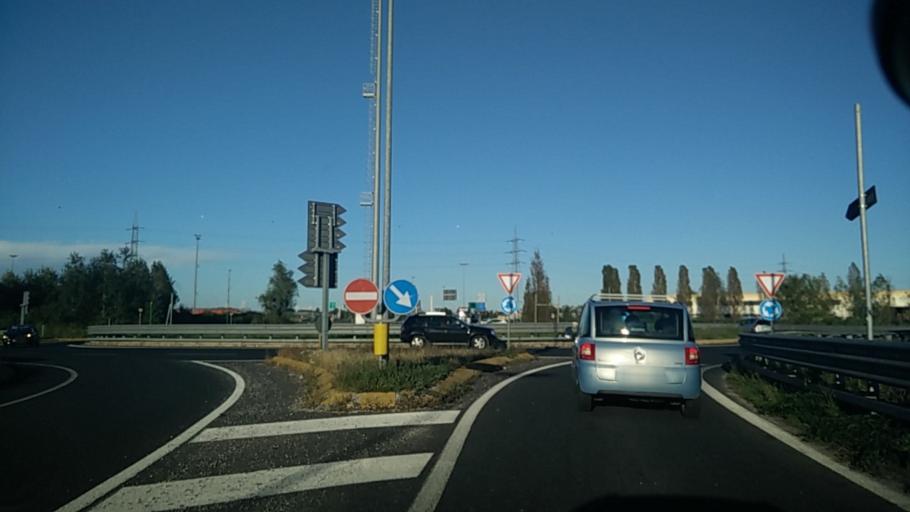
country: IT
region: Veneto
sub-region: Provincia di Venezia
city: Fornase
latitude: 45.4628
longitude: 12.1684
